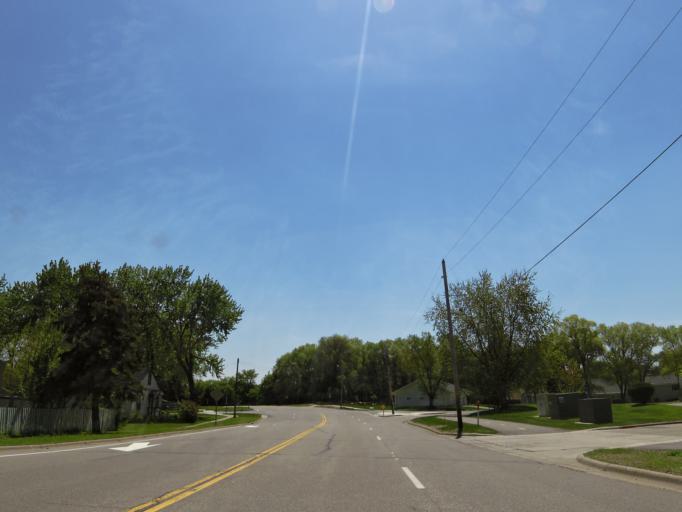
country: US
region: Minnesota
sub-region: Scott County
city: Savage
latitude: 44.8125
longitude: -93.3790
